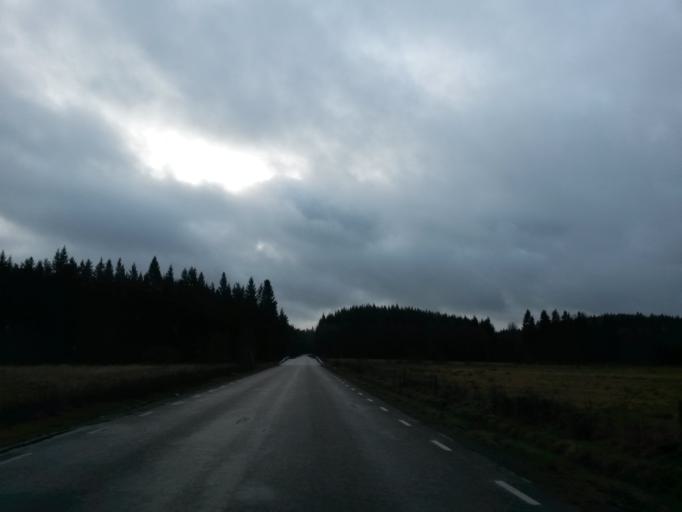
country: SE
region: Vaestra Goetaland
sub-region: Bollebygds Kommun
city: Bollebygd
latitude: 57.6142
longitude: 12.5971
